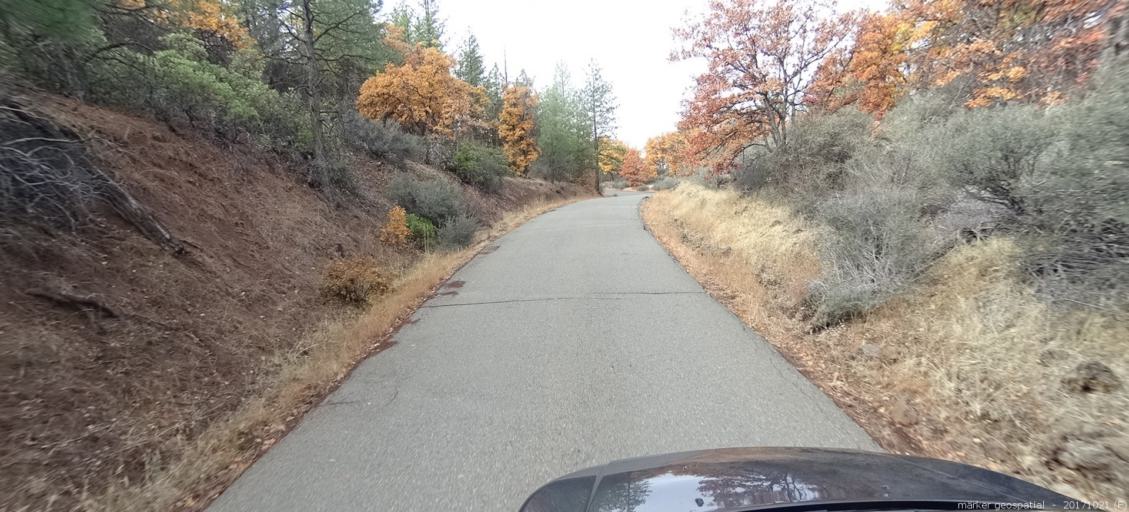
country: US
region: California
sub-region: Shasta County
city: Burney
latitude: 40.9653
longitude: -121.5641
